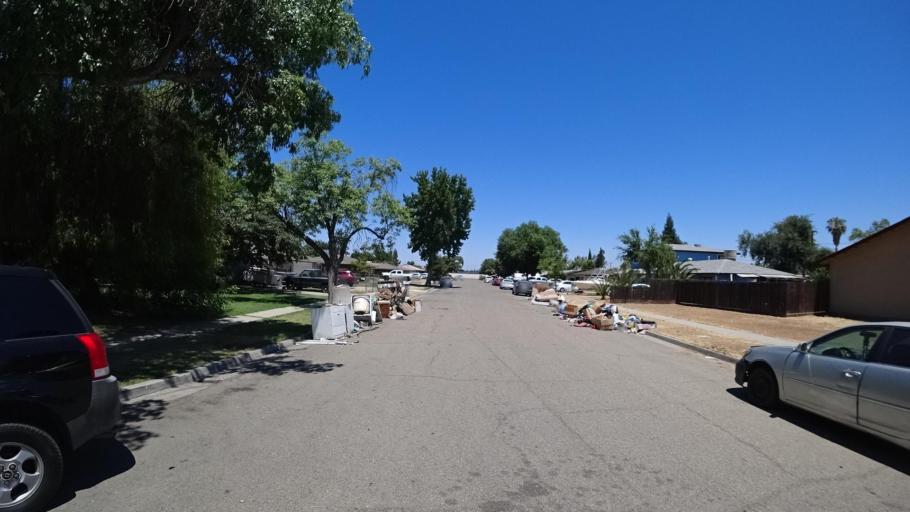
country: US
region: California
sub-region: Fresno County
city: Tarpey Village
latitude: 36.7834
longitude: -119.7420
